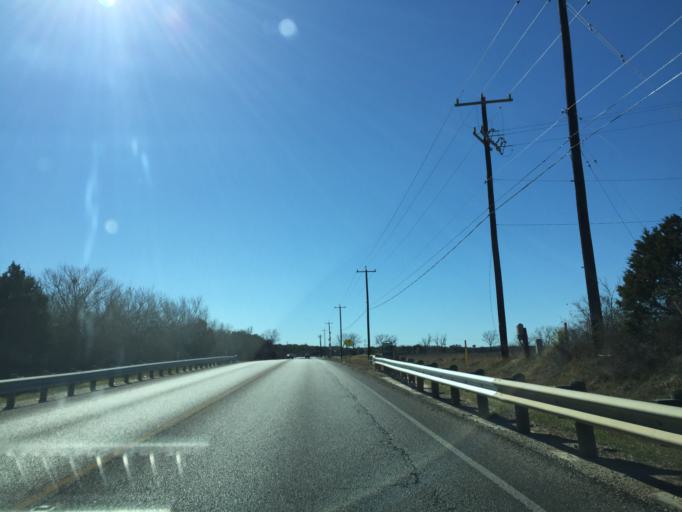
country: US
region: Texas
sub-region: Comal County
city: Bulverde
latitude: 29.7466
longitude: -98.4169
